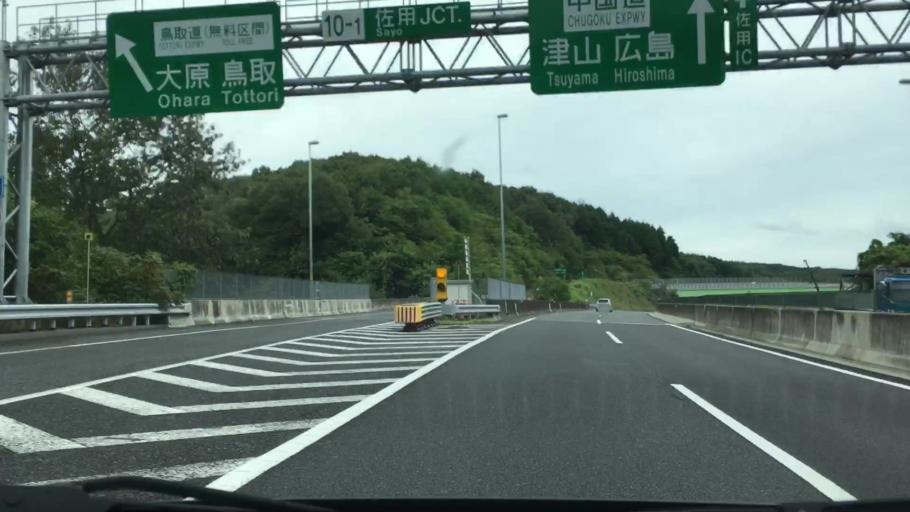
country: JP
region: Hyogo
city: Yamazakicho-nakabirose
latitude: 35.0236
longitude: 134.3946
